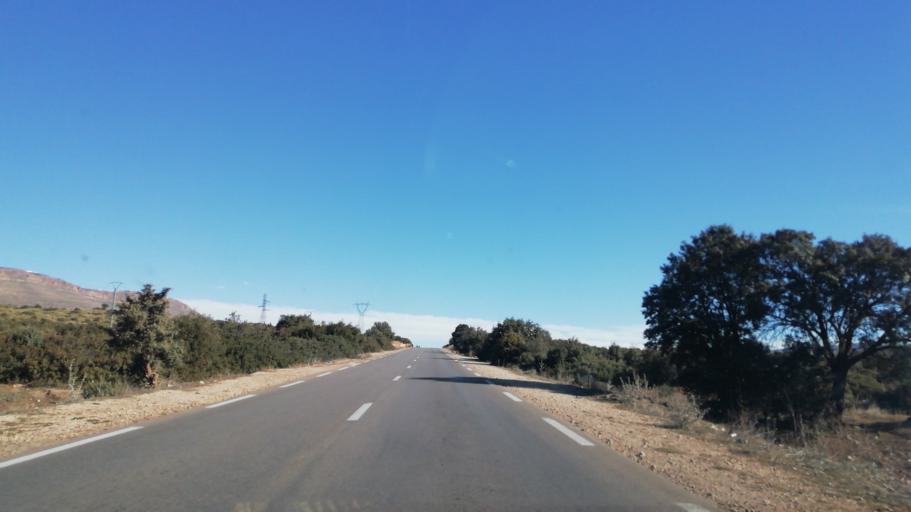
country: DZ
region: Tlemcen
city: Sebdou
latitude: 34.7112
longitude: -1.2108
